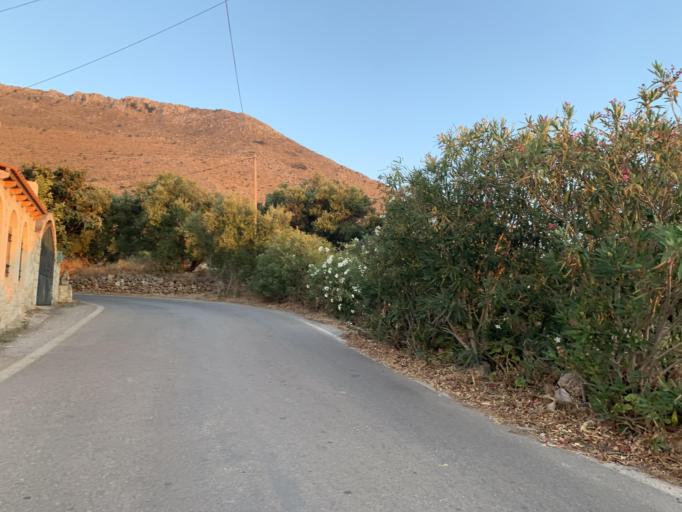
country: GR
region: Crete
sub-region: Nomos Chanias
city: Kalivai
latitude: 35.4523
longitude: 24.2271
